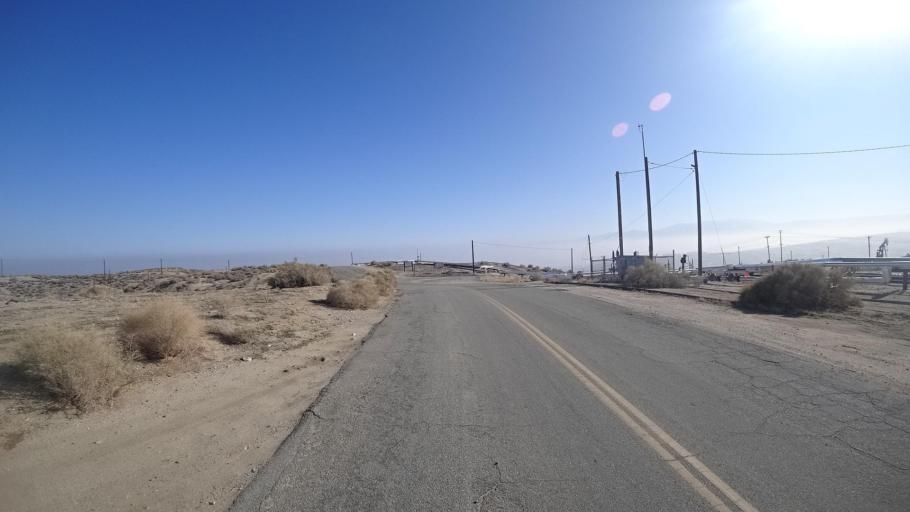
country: US
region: California
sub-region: Kern County
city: South Taft
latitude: 35.1153
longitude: -119.4609
